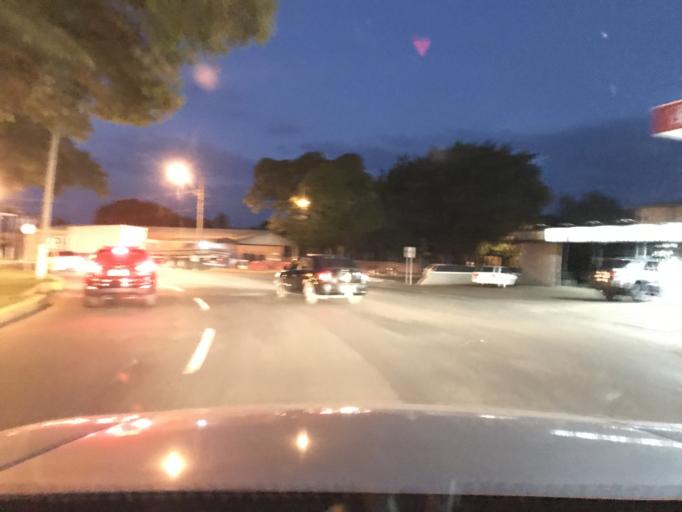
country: PY
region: Canindeyu
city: Salto del Guaira
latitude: -24.0838
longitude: -54.2449
